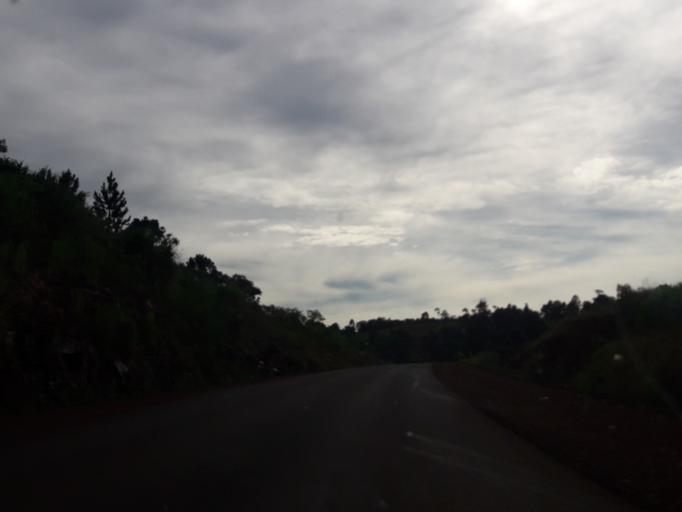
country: AR
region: Misiones
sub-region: Departamento de San Pedro
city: San Pedro
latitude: -26.5126
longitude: -53.9302
